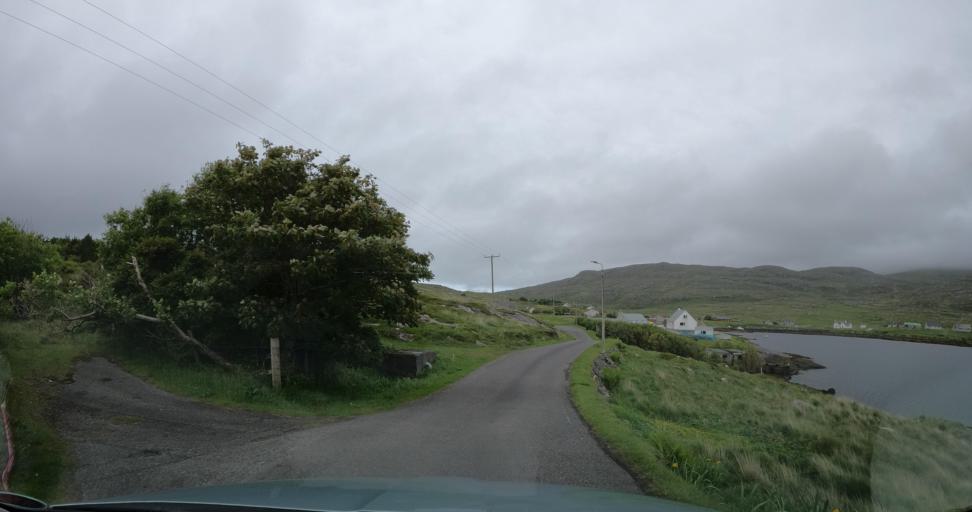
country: GB
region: Scotland
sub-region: Eilean Siar
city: Barra
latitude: 56.9547
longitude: -7.5071
